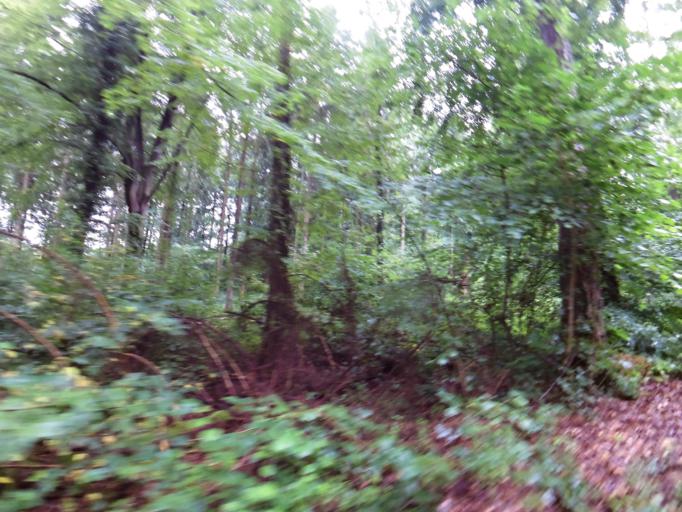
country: BE
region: Wallonia
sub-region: Province de Namur
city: Rochefort
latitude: 50.1491
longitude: 5.2098
